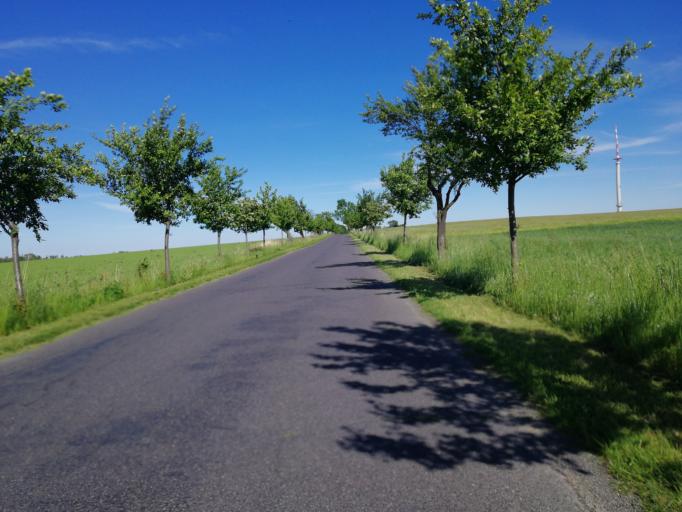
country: DE
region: Brandenburg
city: Calau
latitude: 51.7462
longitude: 13.9274
